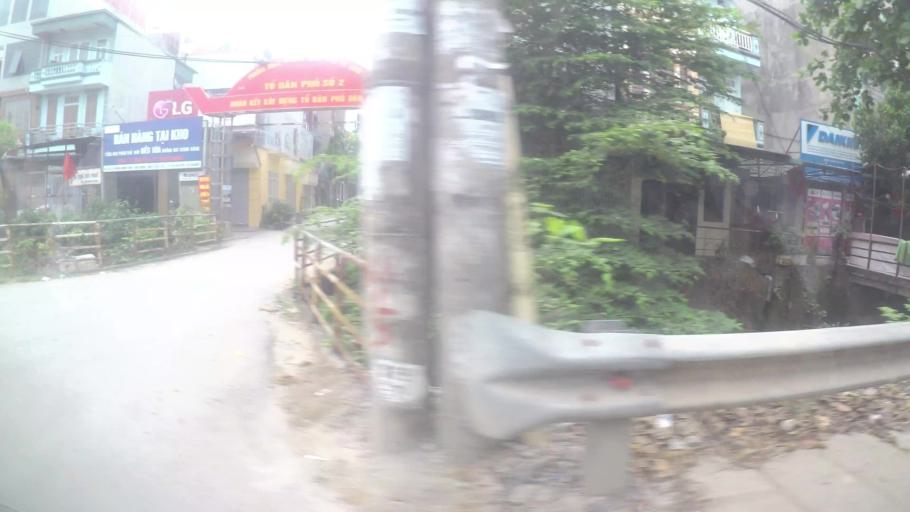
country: VN
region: Ha Noi
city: Cau Dien
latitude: 21.0366
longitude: 105.7558
